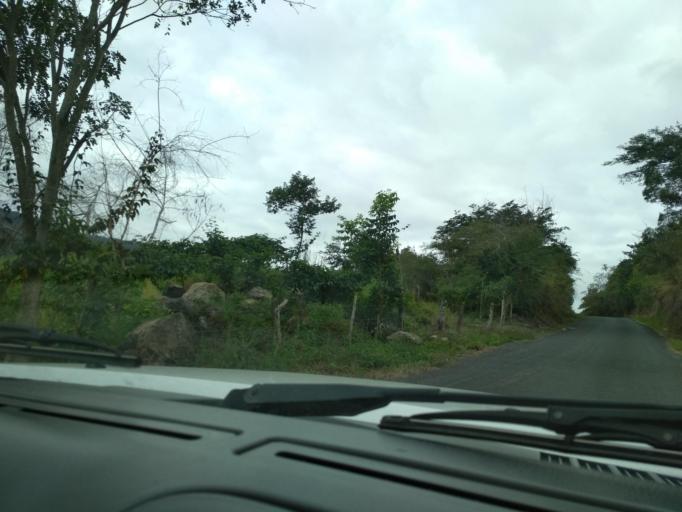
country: MX
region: Veracruz
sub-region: Actopan
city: Trapiche del Rosario
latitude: 19.5660
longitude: -96.7905
